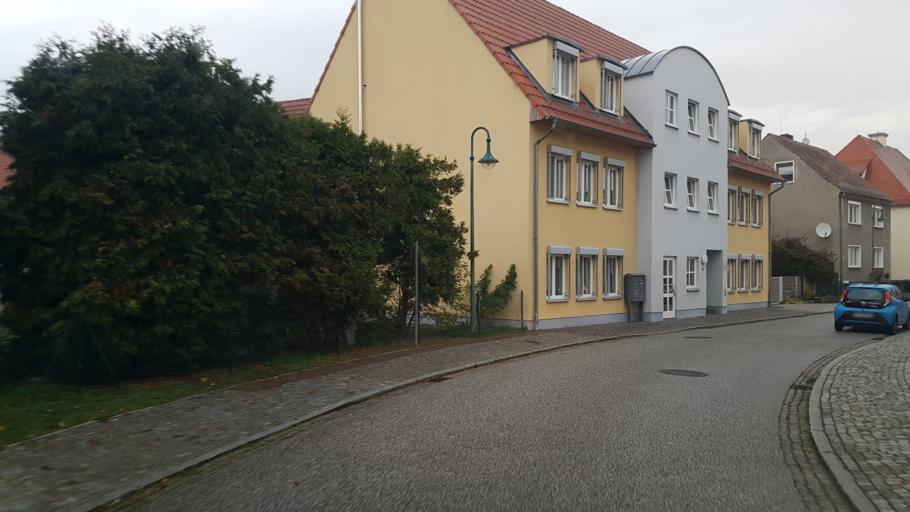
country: DE
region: Brandenburg
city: Schlieben
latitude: 51.7224
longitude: 13.3822
